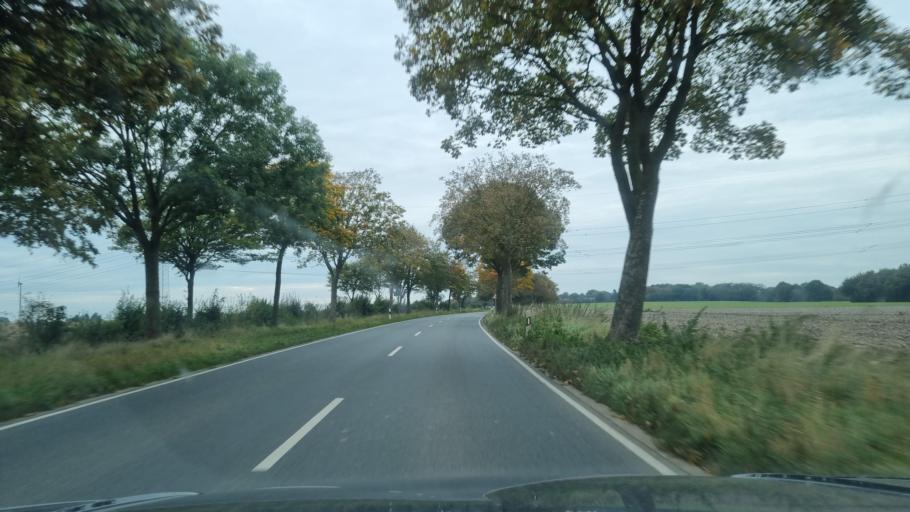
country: DE
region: North Rhine-Westphalia
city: Kalkar
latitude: 51.7129
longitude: 6.3077
